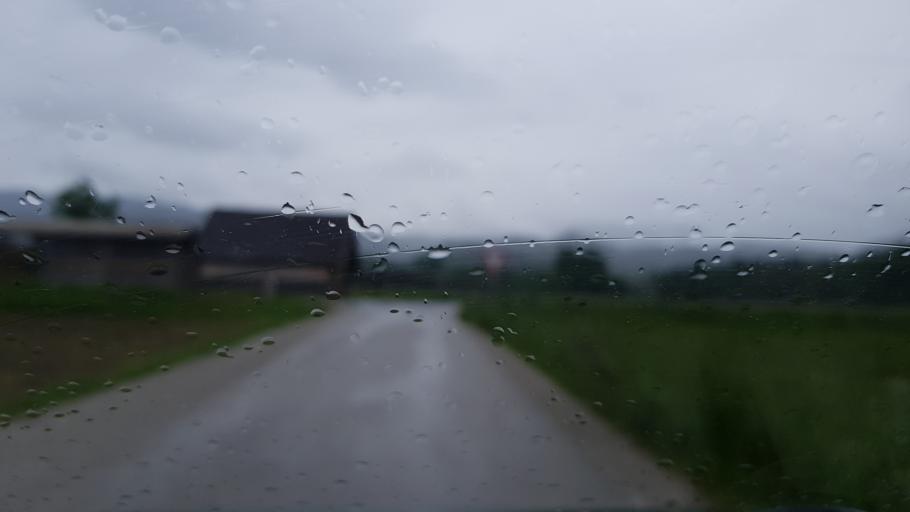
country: SI
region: Bled
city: Zasip
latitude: 46.3851
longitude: 14.1093
